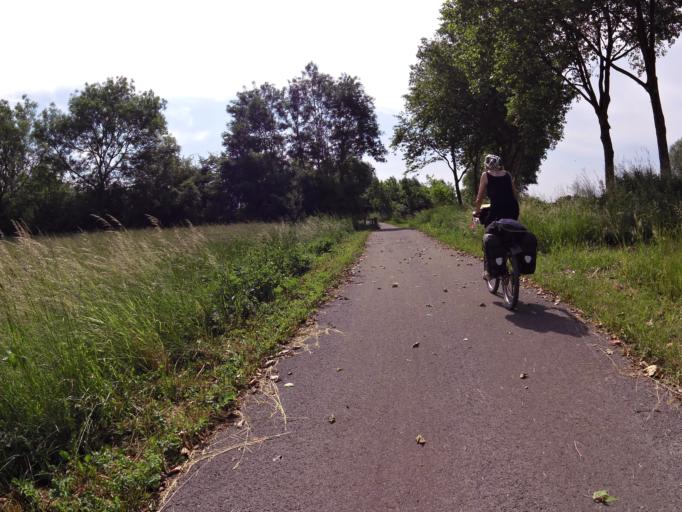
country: FR
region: Champagne-Ardenne
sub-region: Departement de l'Aube
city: Lusigny-sur-Barse
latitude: 48.2671
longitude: 4.2162
